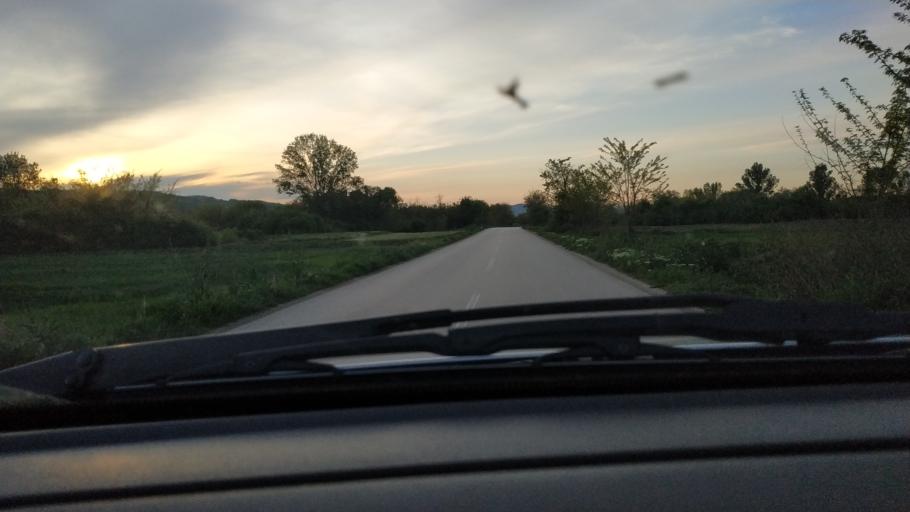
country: RS
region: Central Serbia
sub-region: Nisavski Okrug
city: Aleksinac
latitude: 43.5487
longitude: 21.6206
